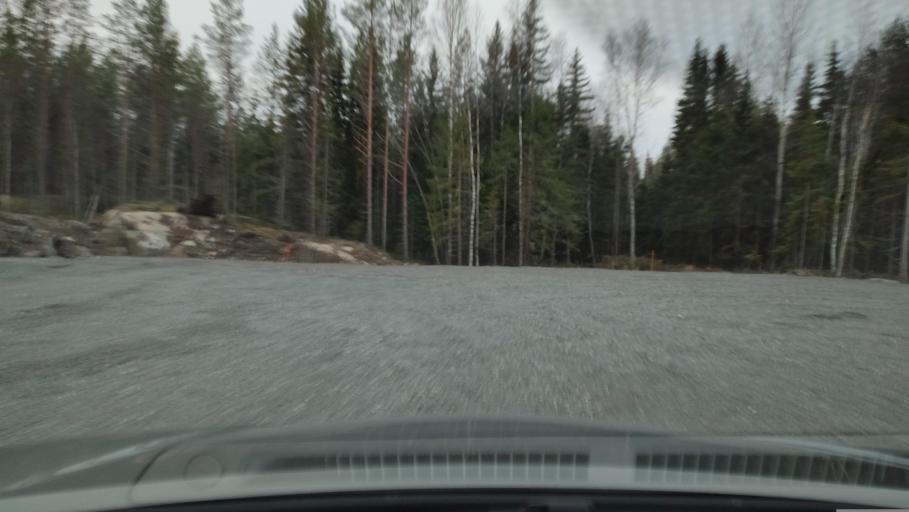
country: FI
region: Southern Ostrobothnia
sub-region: Suupohja
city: Karijoki
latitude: 62.1798
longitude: 21.5703
